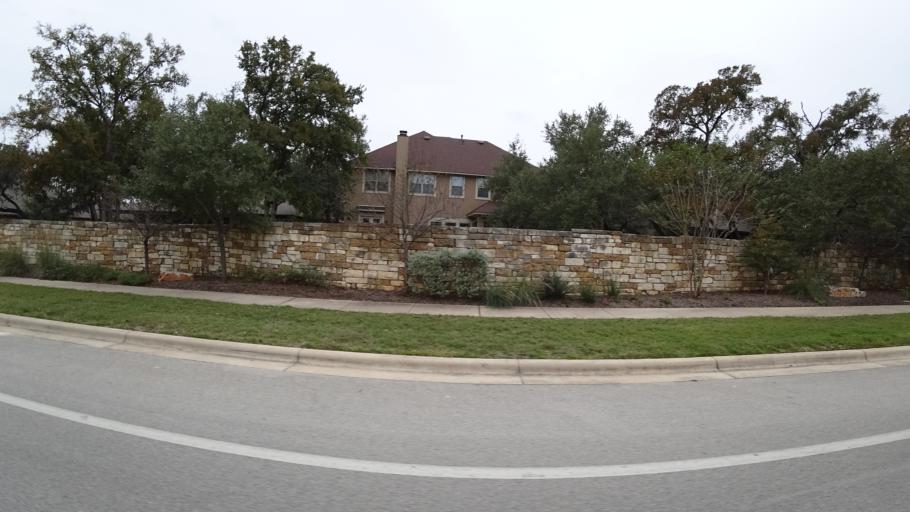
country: US
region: Texas
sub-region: Travis County
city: Shady Hollow
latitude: 30.1966
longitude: -97.9152
